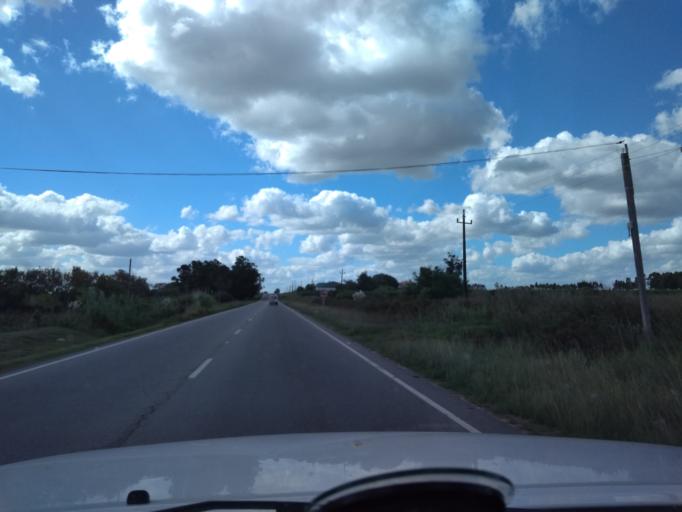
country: UY
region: Canelones
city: Joaquin Suarez
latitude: -34.6989
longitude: -56.0566
